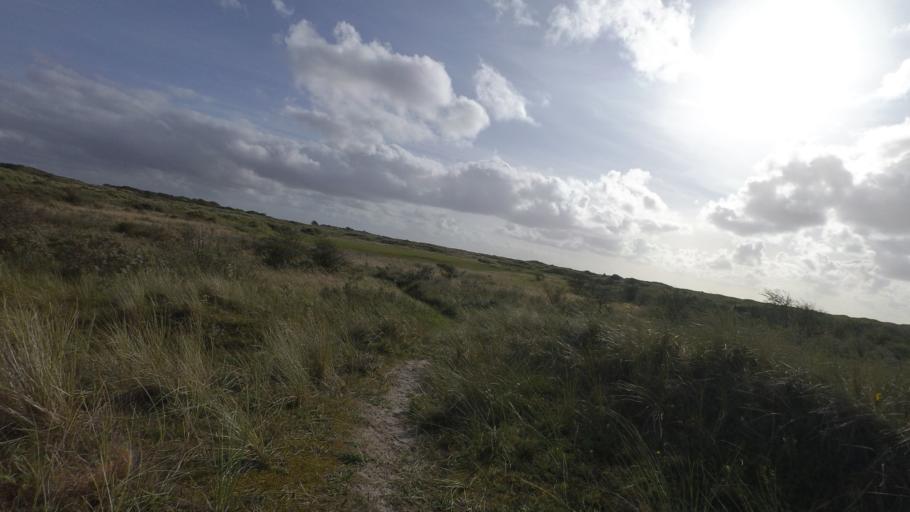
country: NL
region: Friesland
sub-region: Gemeente Ameland
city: Nes
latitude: 53.4554
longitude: 5.8378
